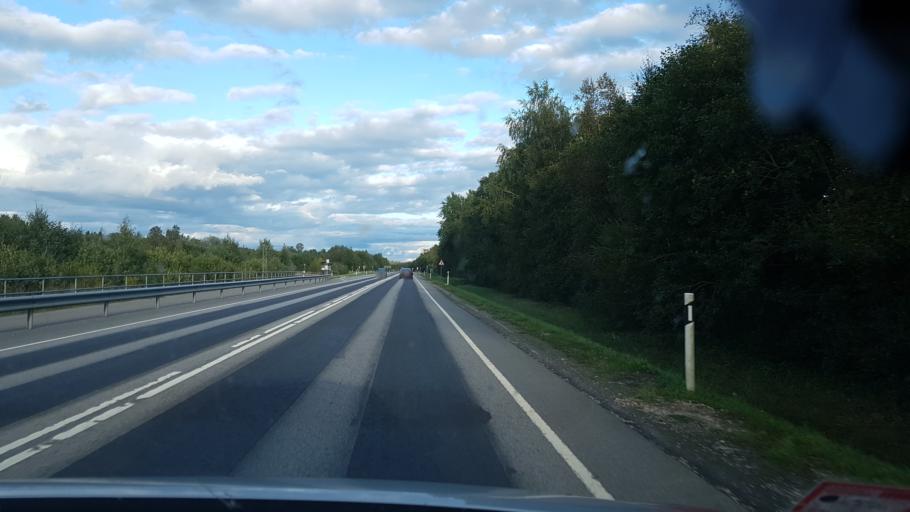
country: EE
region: Laeaene
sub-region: Ridala Parish
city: Uuemoisa
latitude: 58.9492
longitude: 23.6342
